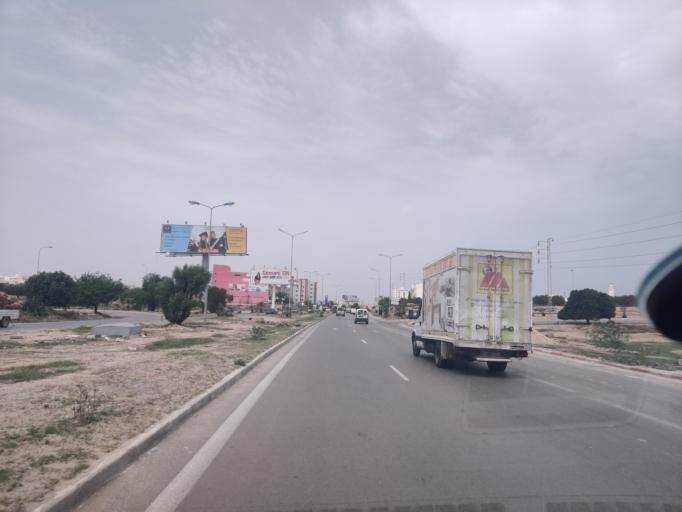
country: TN
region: Susah
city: Hammam Sousse
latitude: 35.8266
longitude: 10.5913
